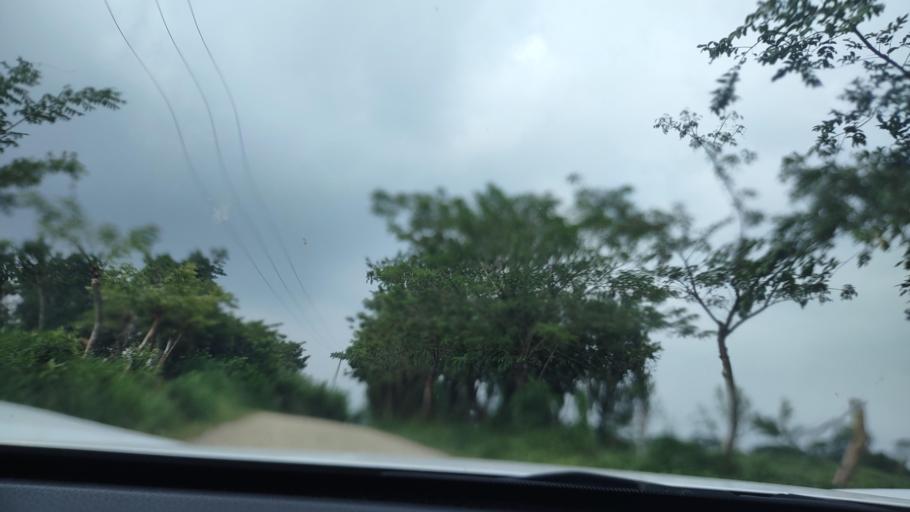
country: MX
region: Veracruz
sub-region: Uxpanapa
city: Poblado 10
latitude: 17.5225
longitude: -94.3015
